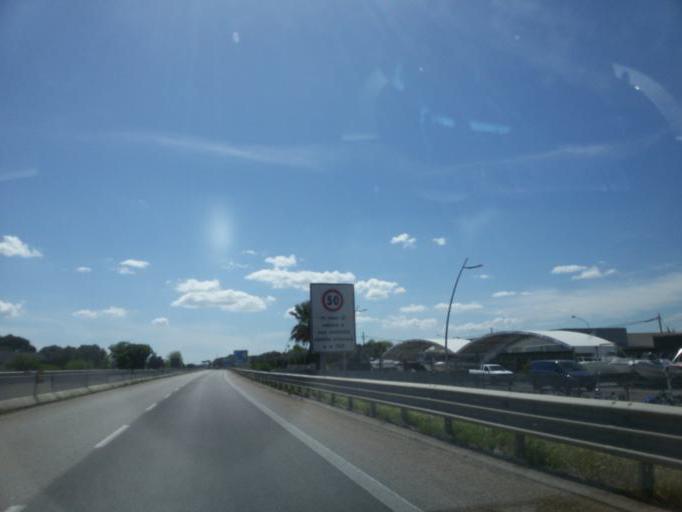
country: IT
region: Apulia
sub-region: Provincia di Brindisi
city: Mesagne
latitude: 40.5738
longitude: 17.8304
